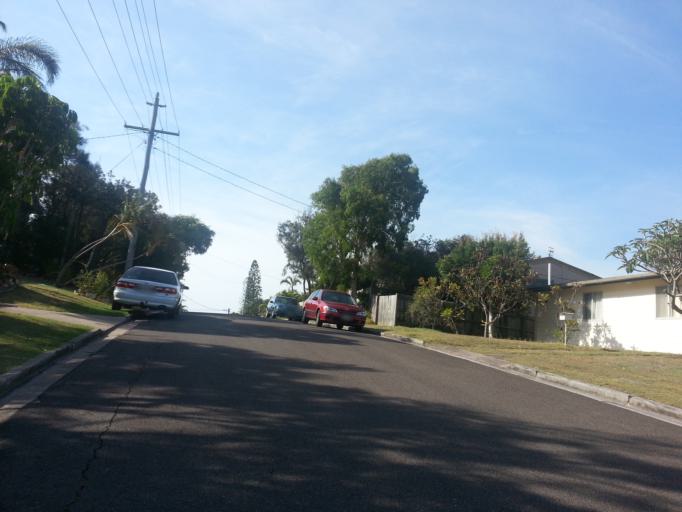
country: AU
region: Queensland
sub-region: Sunshine Coast
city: Peregian Springs
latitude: -26.4938
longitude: 153.0939
